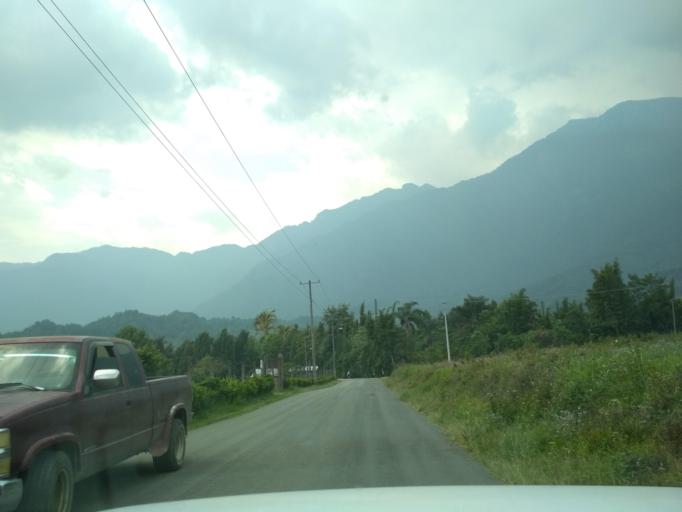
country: MX
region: Veracruz
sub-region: Mariano Escobedo
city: Mariano Escobedo
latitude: 18.9146
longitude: -97.1353
